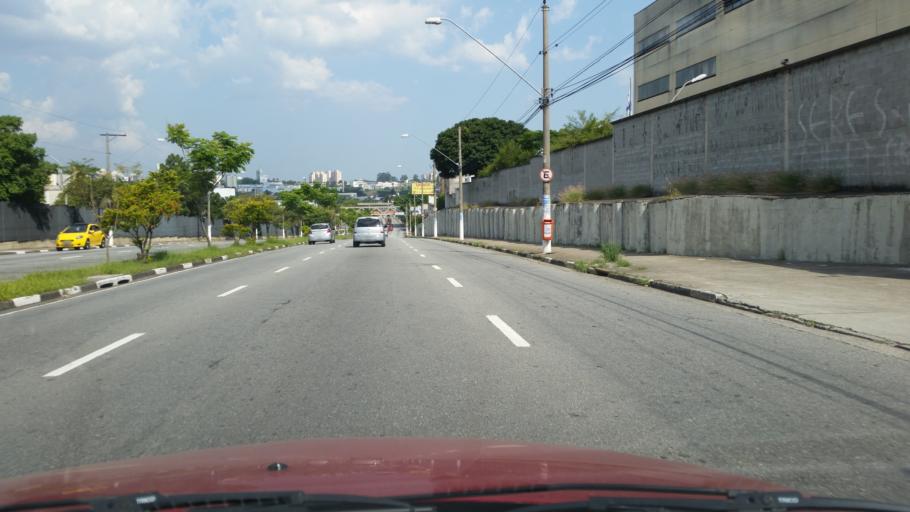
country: BR
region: Sao Paulo
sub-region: Sao Bernardo Do Campo
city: Sao Bernardo do Campo
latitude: -23.6647
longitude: -46.5875
